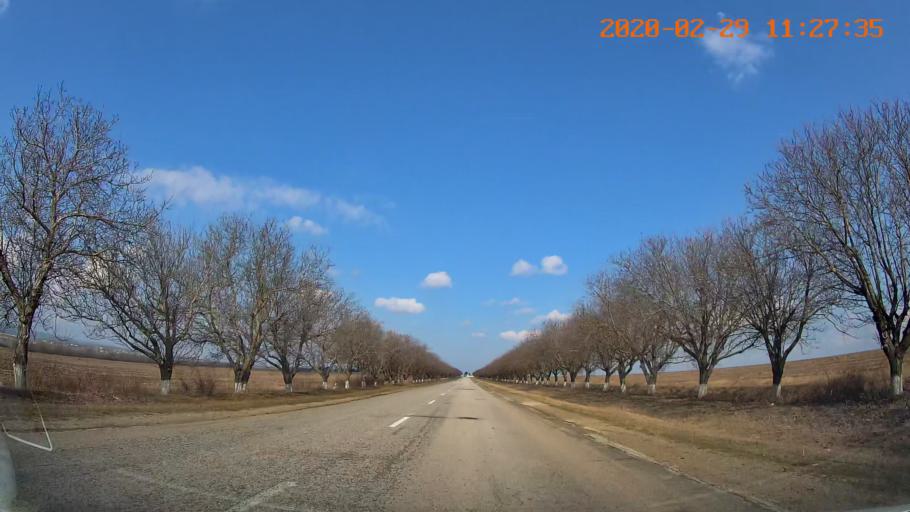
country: MD
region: Telenesti
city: Cocieri
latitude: 47.4706
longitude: 29.1419
